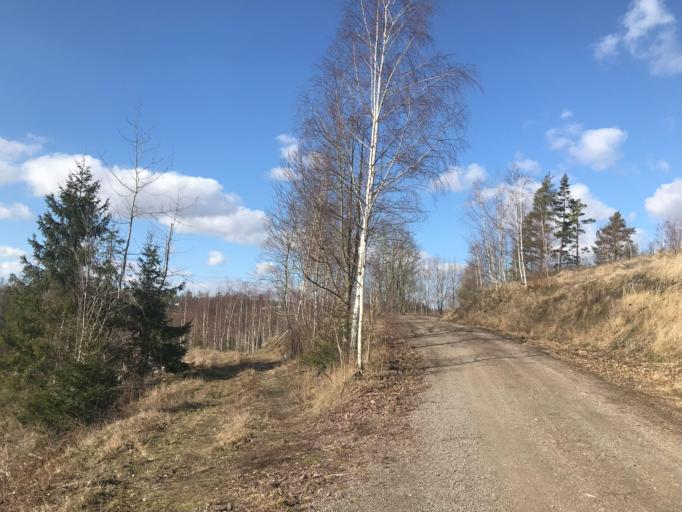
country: DE
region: Saxony-Anhalt
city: Harzgerode
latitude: 51.6338
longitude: 11.1005
